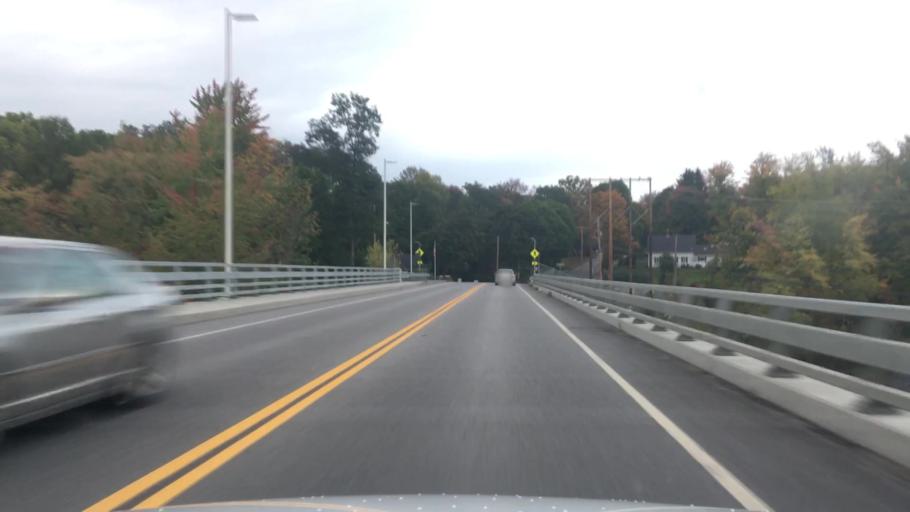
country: US
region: Maine
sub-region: York County
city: Buxton
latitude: 43.6128
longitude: -70.5517
